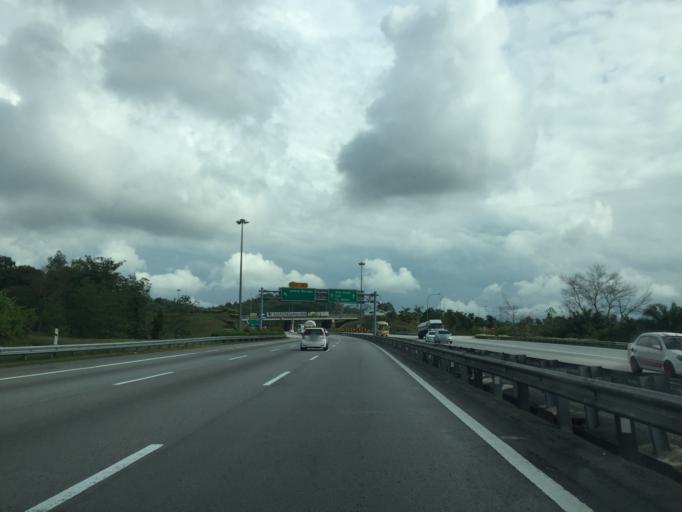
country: MY
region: Selangor
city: Batang Berjuntai
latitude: 3.5748
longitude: 101.5244
